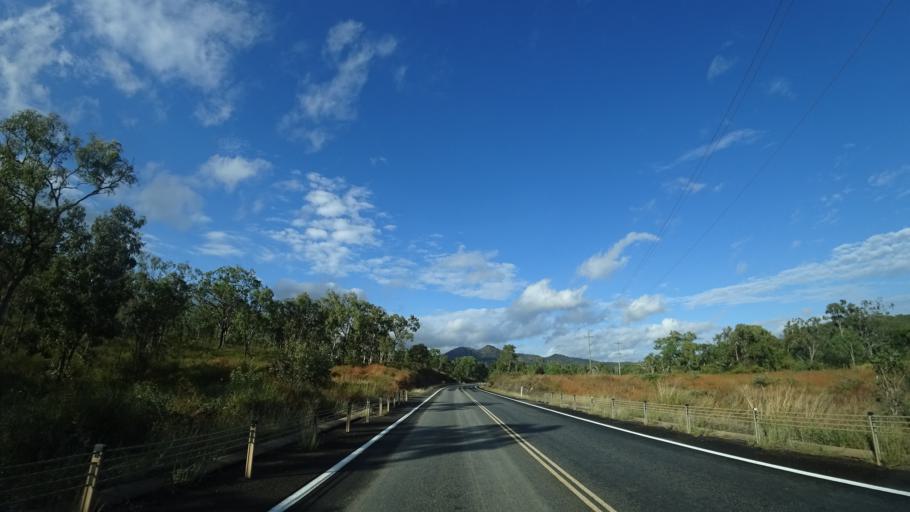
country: AU
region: Queensland
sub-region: Cook
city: Cooktown
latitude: -15.6147
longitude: 145.2211
